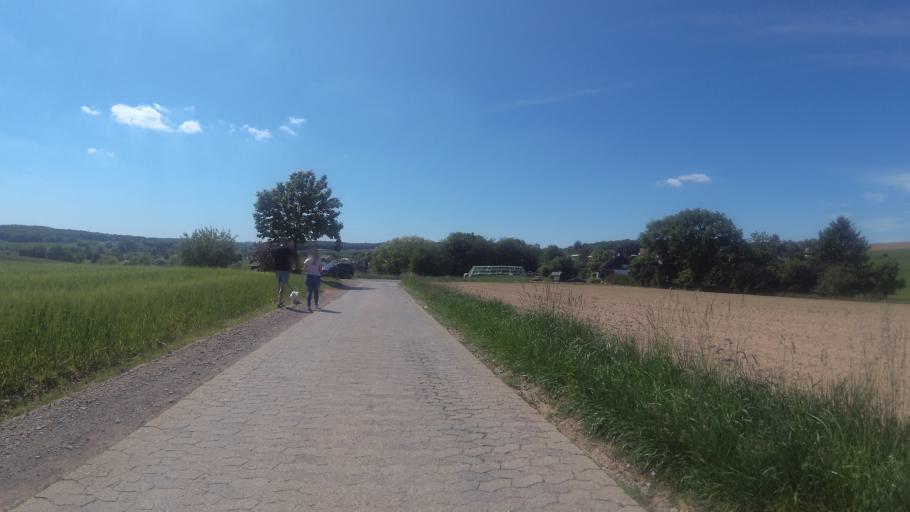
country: DE
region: Saarland
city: Heusweiler
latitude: 49.3476
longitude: 6.9030
